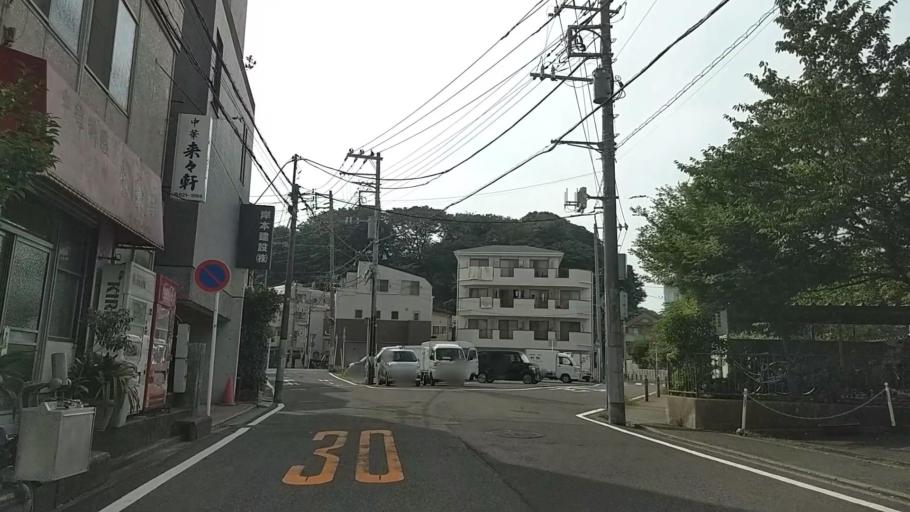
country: JP
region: Kanagawa
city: Yokohama
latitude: 35.4314
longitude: 139.6640
